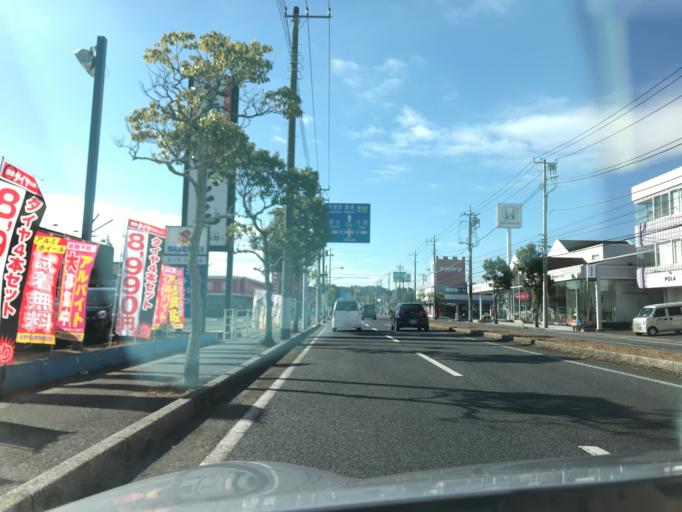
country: JP
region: Chiba
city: Mobara
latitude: 35.4390
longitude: 140.2889
